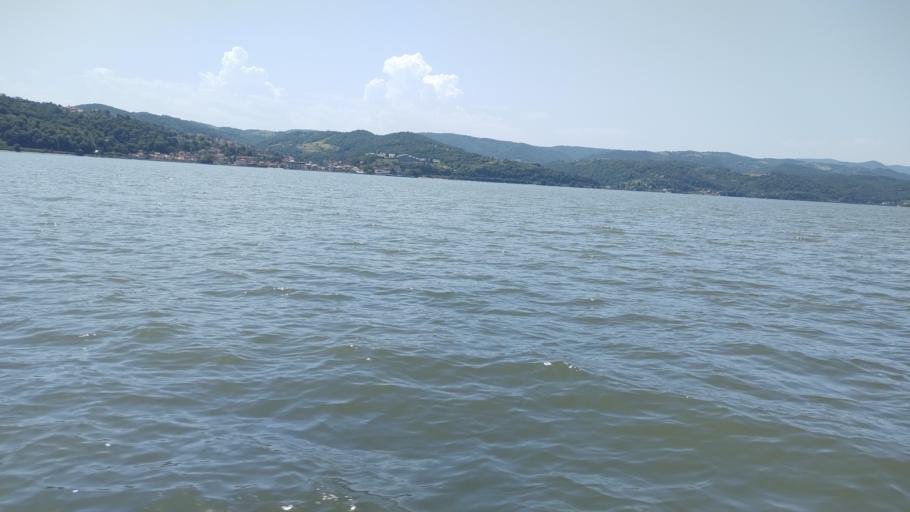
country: RO
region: Mehedinti
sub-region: Comuna Svinita
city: Svinita
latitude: 44.4794
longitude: 22.1602
